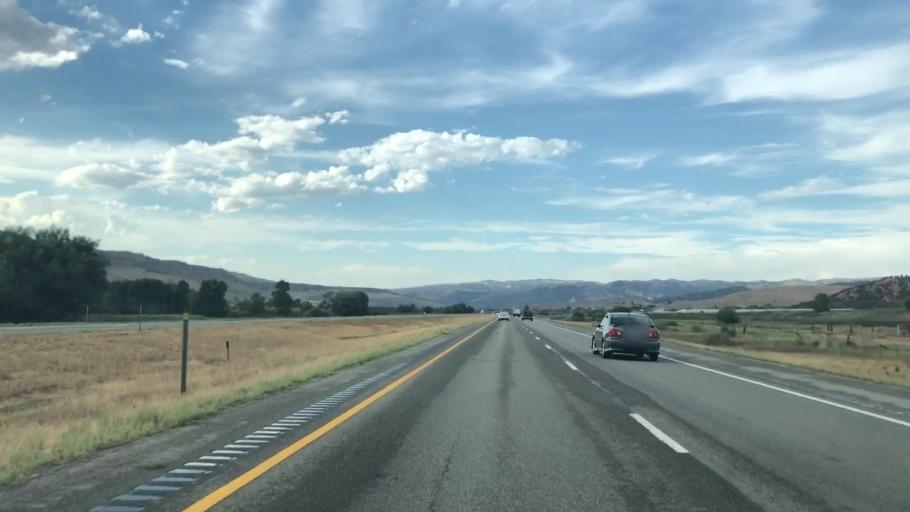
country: US
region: Utah
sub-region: Summit County
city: Coalville
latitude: 40.8780
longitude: -111.3920
